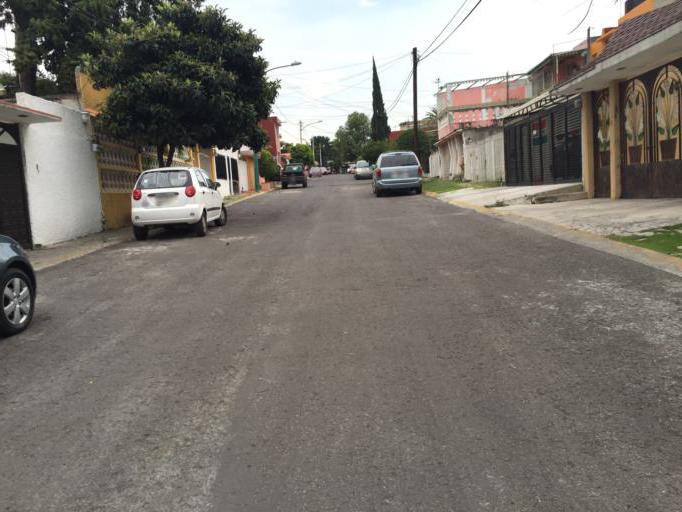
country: MX
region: Mexico
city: Cuautitlan Izcalli
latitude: 19.6507
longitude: -99.2175
